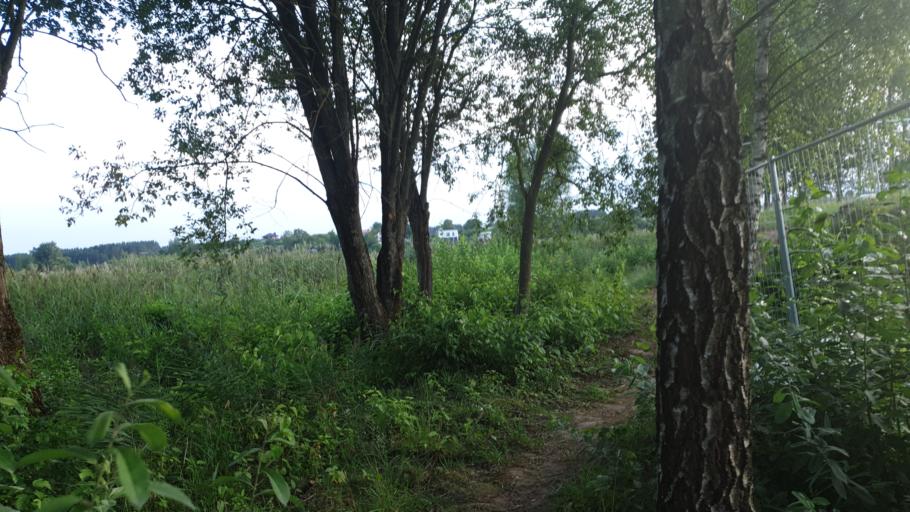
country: LT
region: Vilnius County
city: Pilaite
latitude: 54.7045
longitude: 25.1625
